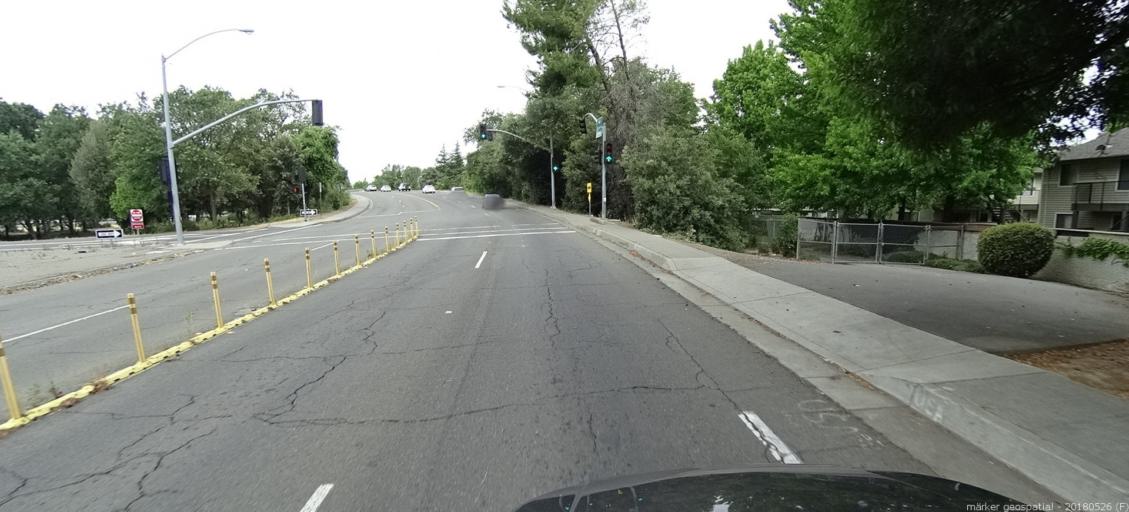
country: US
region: California
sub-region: Sacramento County
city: Sacramento
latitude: 38.6146
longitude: -121.5098
